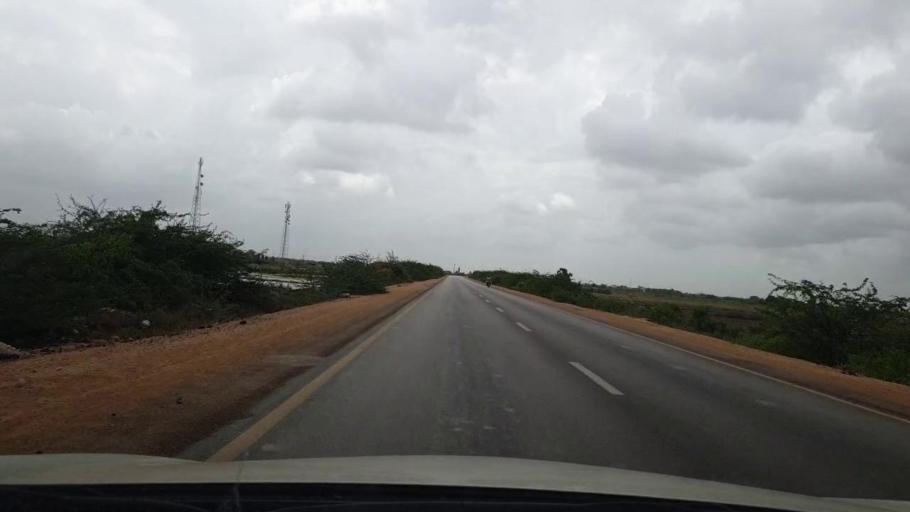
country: PK
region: Sindh
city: Mirpur Batoro
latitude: 24.6418
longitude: 68.3989
